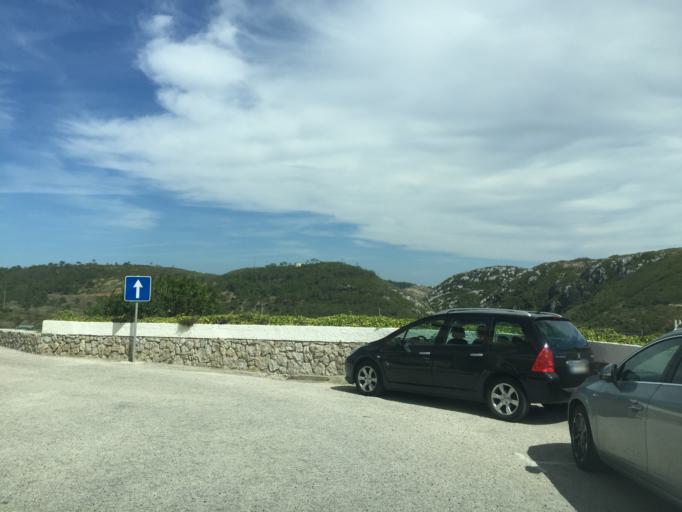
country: PT
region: Lisbon
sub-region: Torres Vedras
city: A dos Cunhados
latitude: 39.1792
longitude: -9.3547
